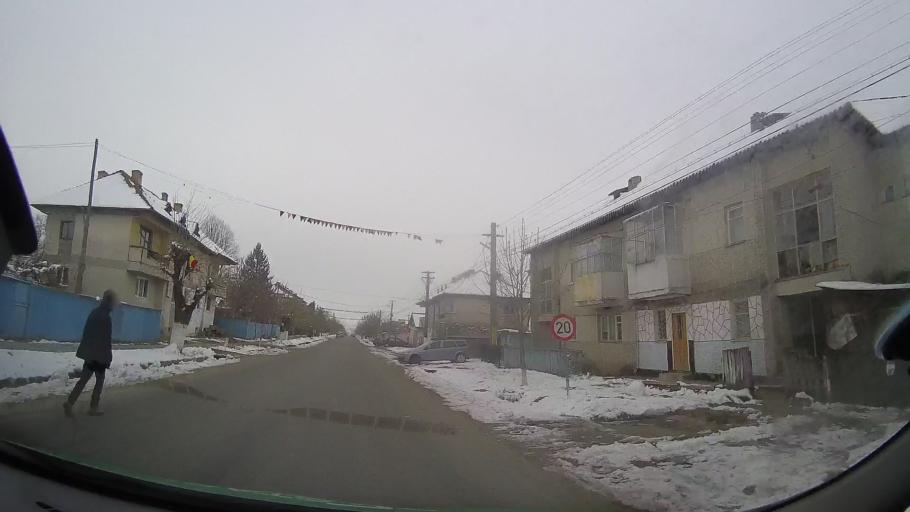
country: RO
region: Bacau
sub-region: Comuna Huruesti
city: Huruesti
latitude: 46.3024
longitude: 27.2961
